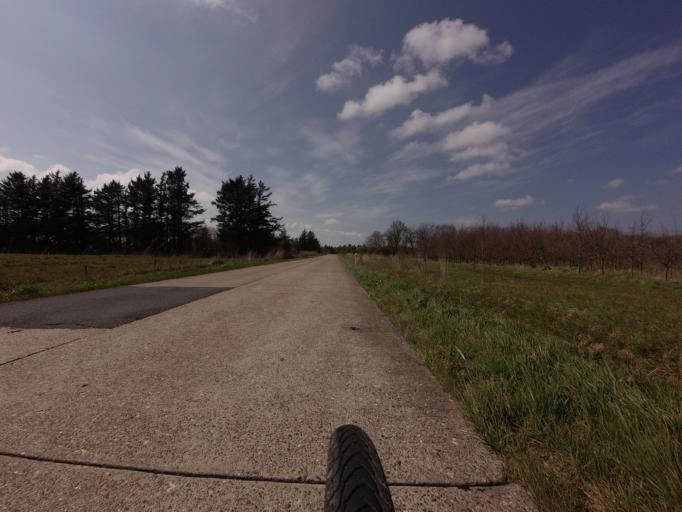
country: DK
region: North Denmark
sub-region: Jammerbugt Kommune
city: Brovst
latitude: 57.1644
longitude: 9.4945
